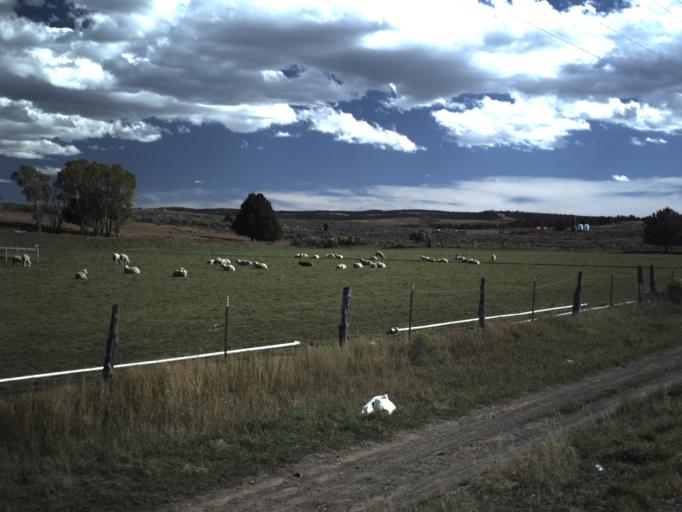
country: US
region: Utah
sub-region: Garfield County
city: Panguitch
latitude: 37.8069
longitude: -112.4353
